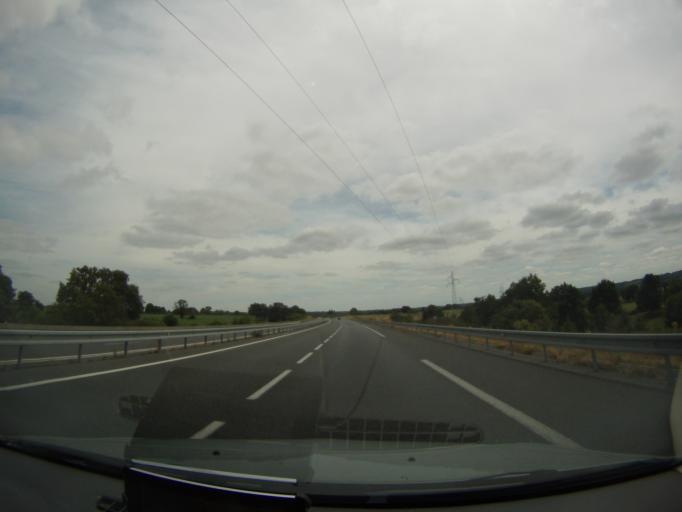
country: FR
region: Pays de la Loire
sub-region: Departement de Maine-et-Loire
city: La Tessoualle
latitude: 46.9737
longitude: -0.8109
